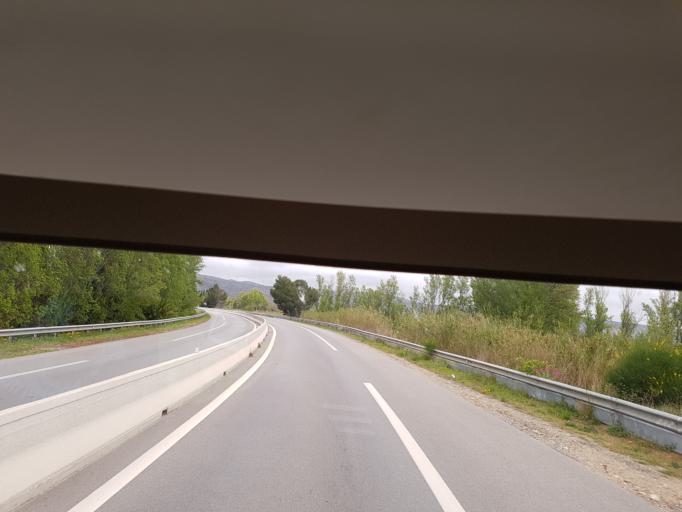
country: FR
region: Languedoc-Roussillon
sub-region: Departement des Pyrenees-Orientales
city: Salses-le-Chateau
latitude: 42.8294
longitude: 2.9243
